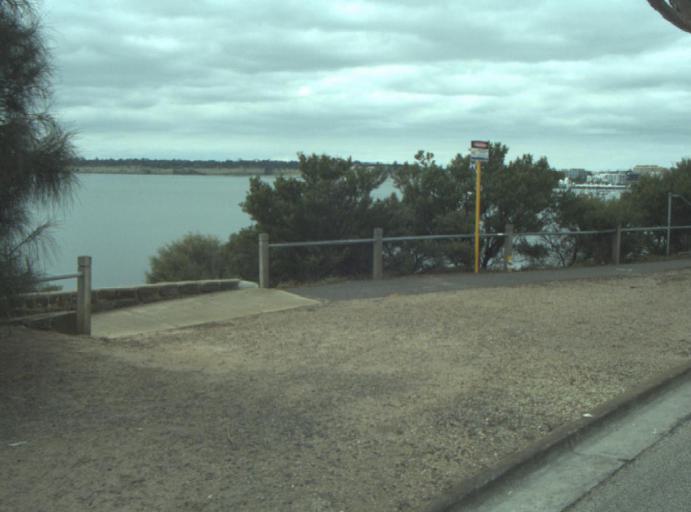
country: AU
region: Victoria
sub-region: Greater Geelong
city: Geelong West
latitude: -38.1295
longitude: 144.3569
